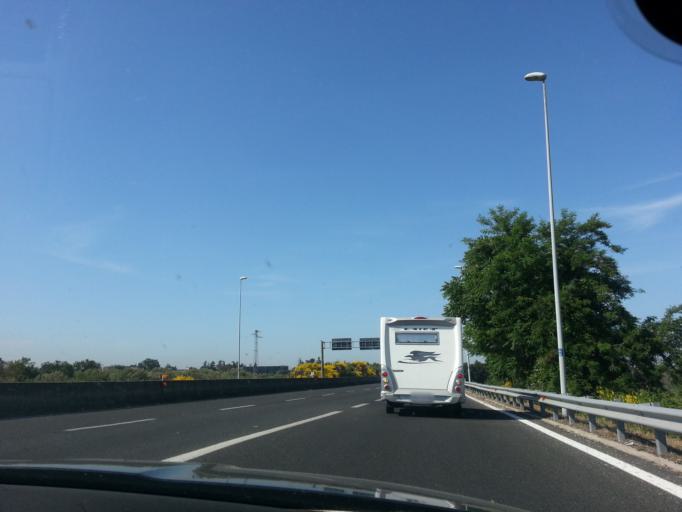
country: IT
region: Latium
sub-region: Provincia di Viterbo
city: Viterbo
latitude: 42.4360
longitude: 12.0893
